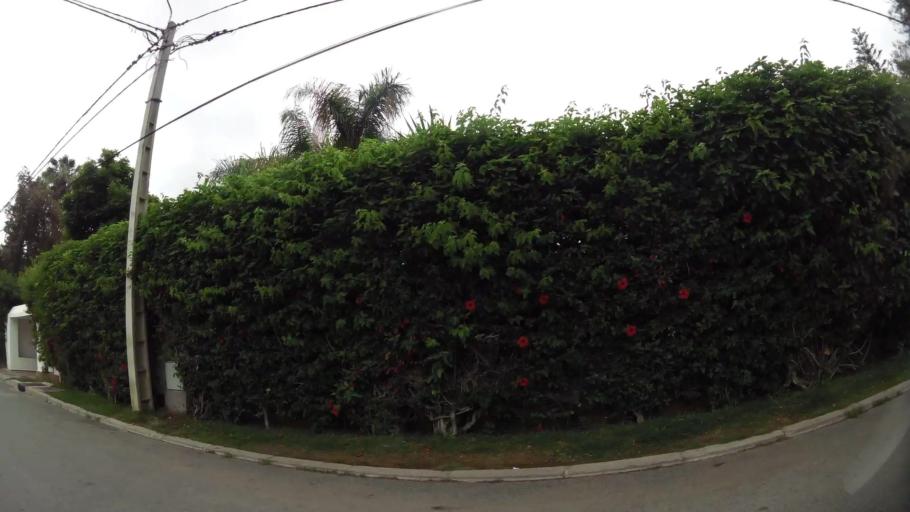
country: MA
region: Rabat-Sale-Zemmour-Zaer
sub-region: Rabat
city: Rabat
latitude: 33.9762
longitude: -6.8280
